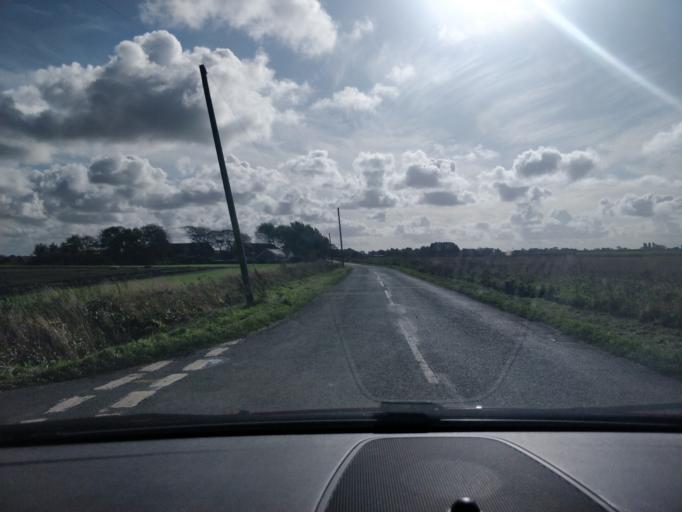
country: GB
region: England
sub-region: Lancashire
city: Banks
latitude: 53.6281
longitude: -2.9414
